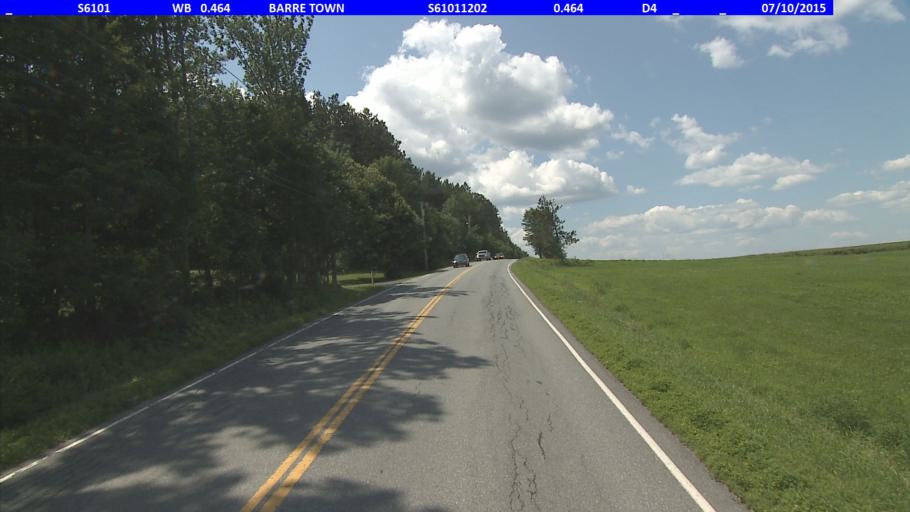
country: US
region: Vermont
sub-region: Washington County
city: South Barre
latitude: 44.1877
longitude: -72.5373
